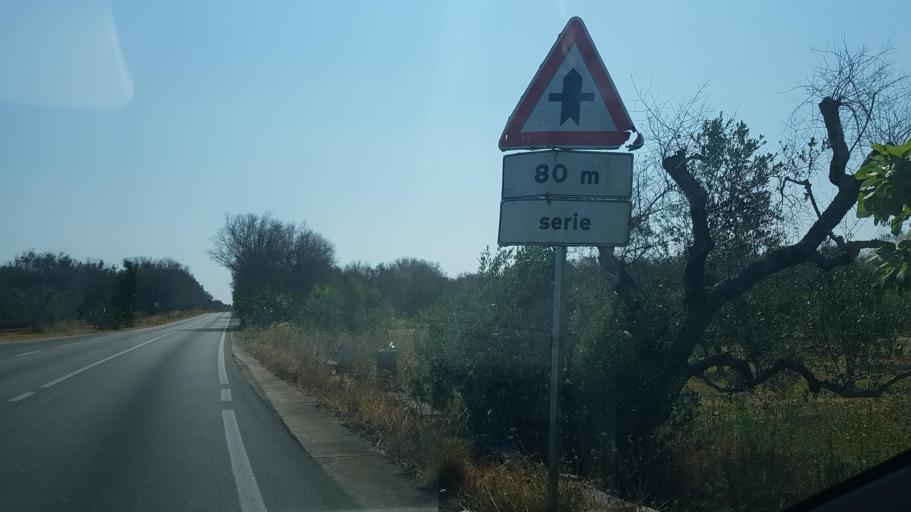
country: IT
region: Apulia
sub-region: Provincia di Lecce
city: Ruffano
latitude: 40.0023
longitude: 18.2817
